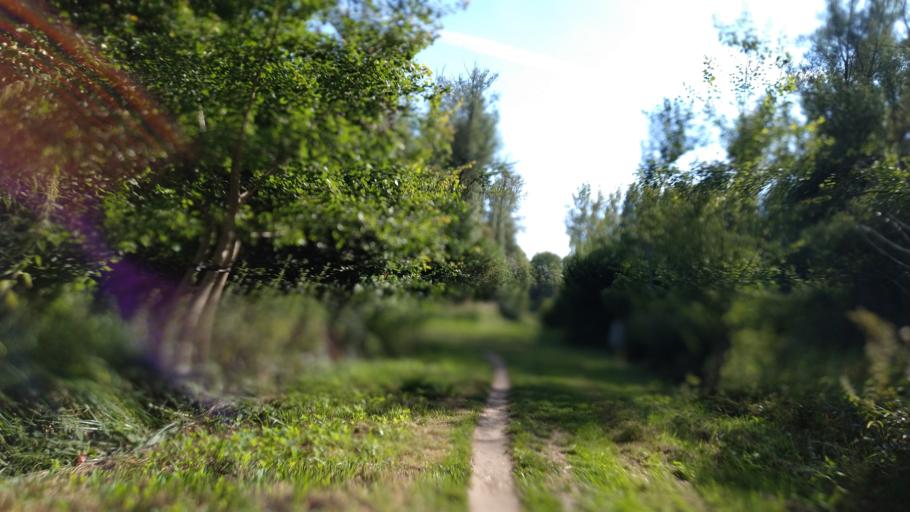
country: BE
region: Flanders
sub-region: Provincie Vlaams-Brabant
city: Oud-Heverlee
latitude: 50.8582
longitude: 4.6622
